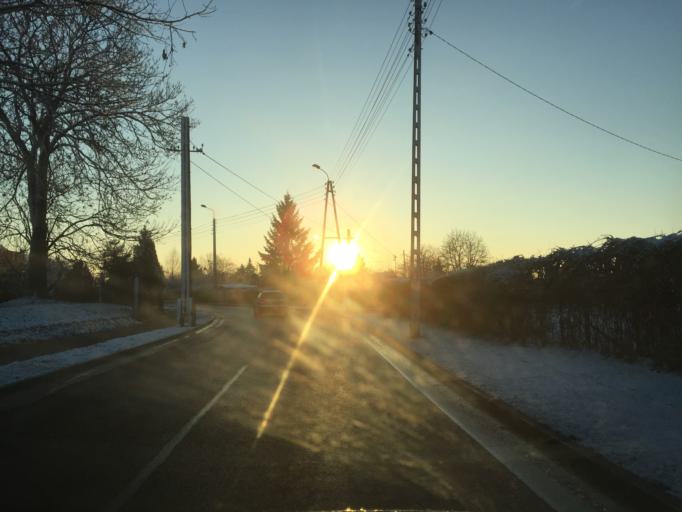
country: PL
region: Kujawsko-Pomorskie
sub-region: Powiat golubsko-dobrzynski
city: Kowalewo Pomorskie
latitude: 53.1533
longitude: 18.8925
